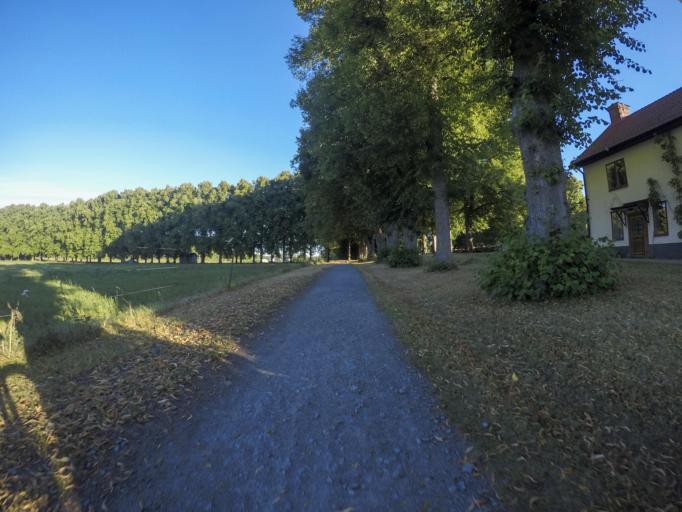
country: SE
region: Vaestmanland
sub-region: Vasteras
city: Vasteras
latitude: 59.5557
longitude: 16.6601
